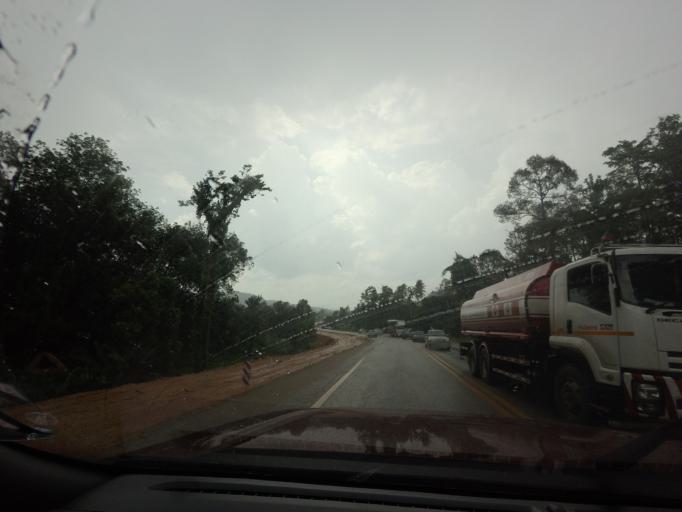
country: TH
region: Yala
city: Krong Pi Nang
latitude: 6.3805
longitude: 101.2964
